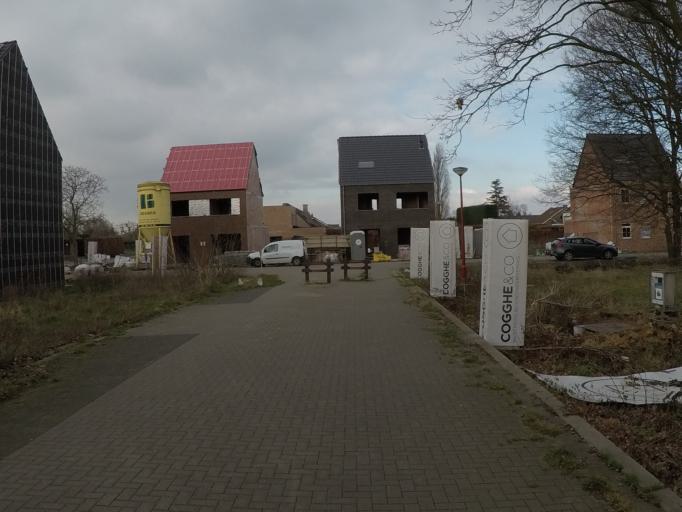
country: BE
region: Flanders
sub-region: Provincie Antwerpen
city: Kapellen
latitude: 51.3121
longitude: 4.4006
